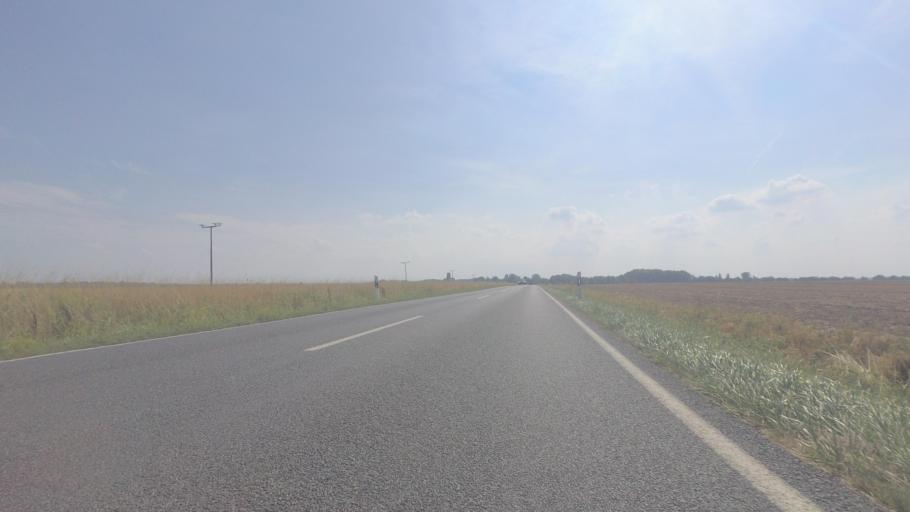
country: DE
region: Mecklenburg-Vorpommern
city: Wittenhagen
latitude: 54.1366
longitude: 13.1460
